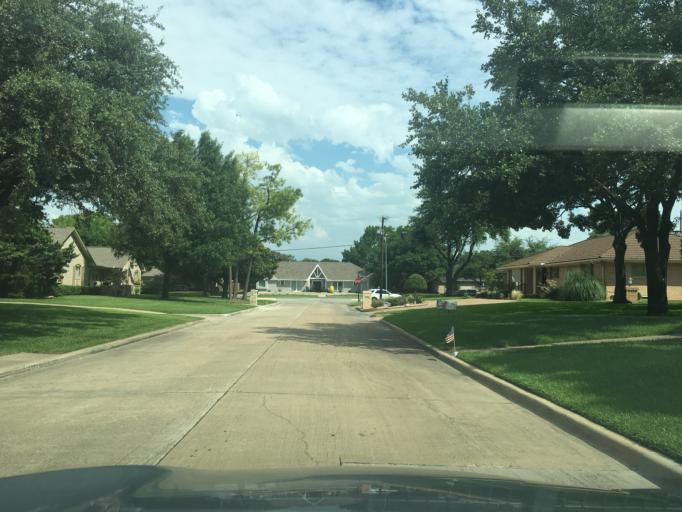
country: US
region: Texas
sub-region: Dallas County
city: Farmers Branch
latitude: 32.9316
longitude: -96.8584
